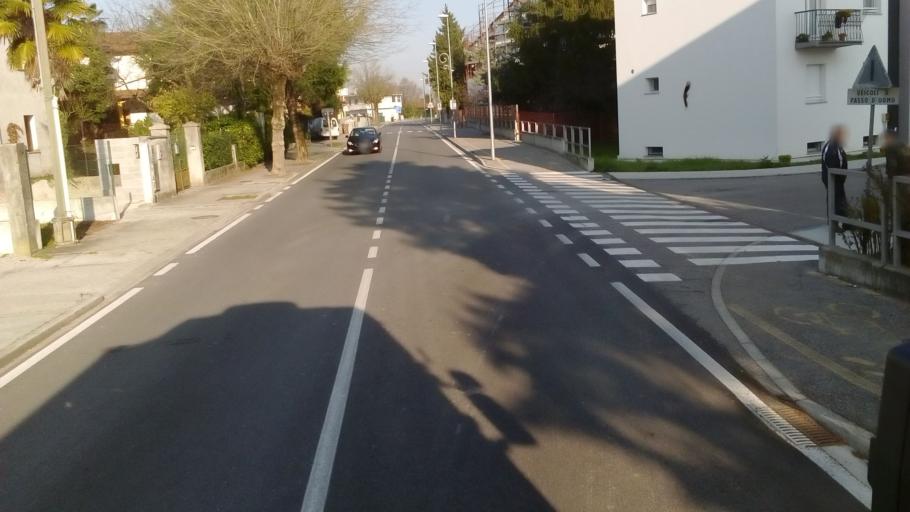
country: IT
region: Friuli Venezia Giulia
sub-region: Provincia di Udine
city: Precenicco
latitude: 45.8037
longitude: 13.0718
